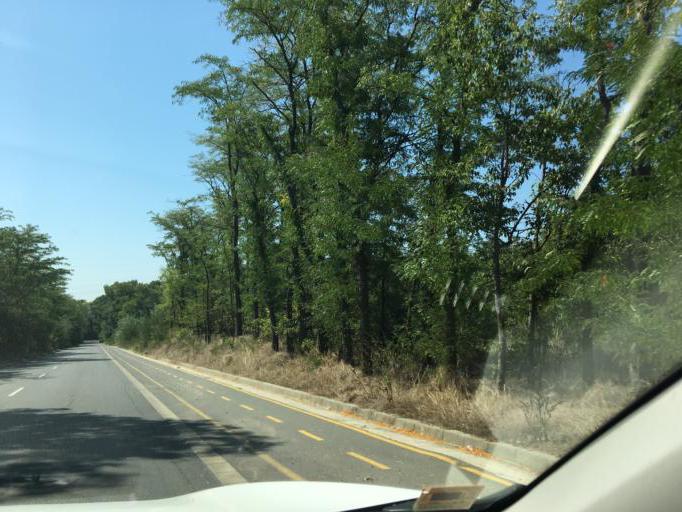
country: BG
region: Burgas
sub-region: Obshtina Kameno
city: Kameno
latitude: 42.6146
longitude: 27.3933
